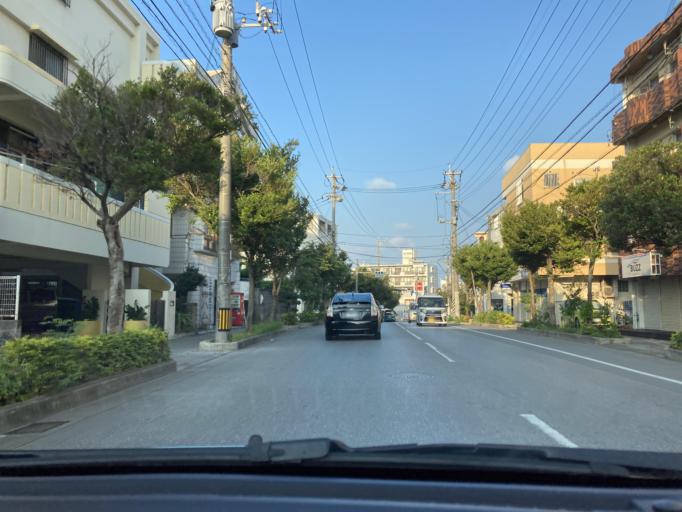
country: JP
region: Okinawa
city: Naha-shi
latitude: 26.2016
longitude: 127.6945
